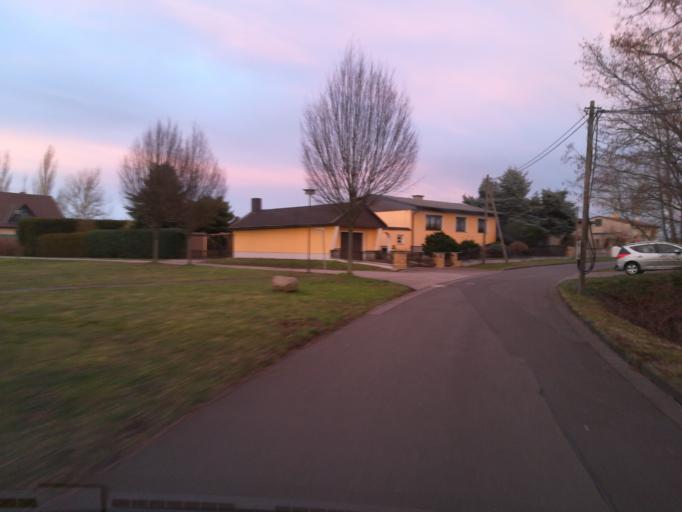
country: DE
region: Saxony-Anhalt
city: Brehna
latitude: 51.5426
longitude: 12.2237
